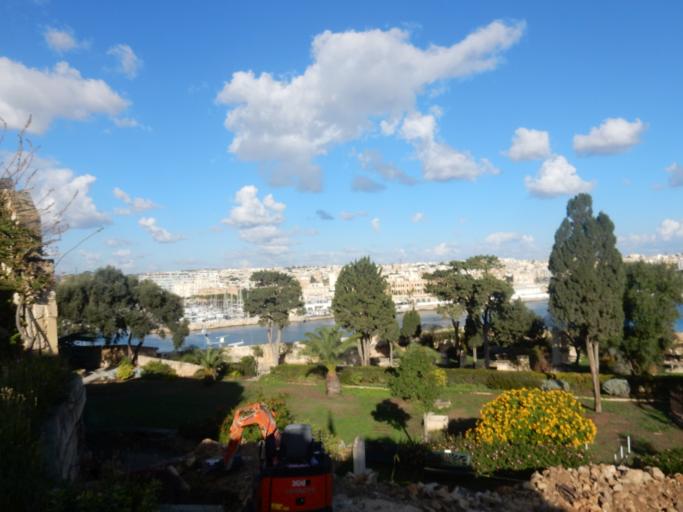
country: MT
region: Il-Furjana
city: Floriana
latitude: 35.8956
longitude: 14.5022
